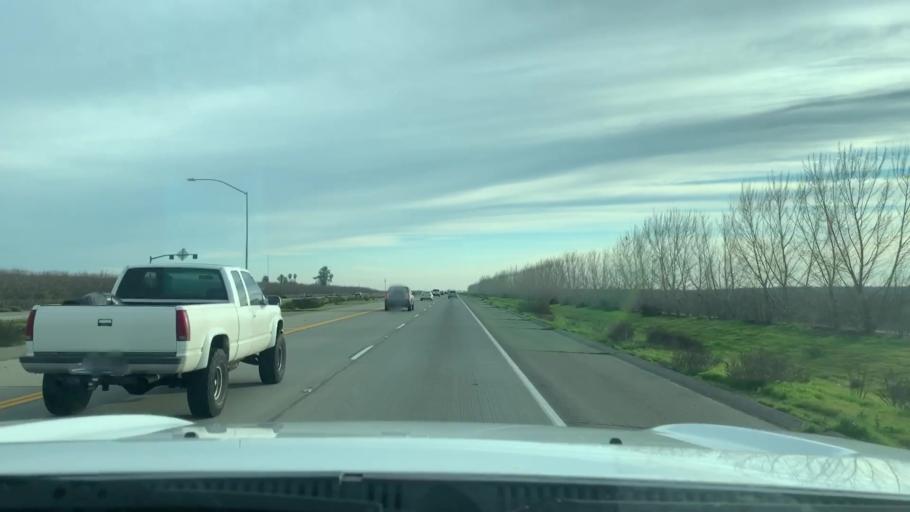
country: US
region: California
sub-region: Fresno County
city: Caruthers
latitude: 36.5167
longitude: -119.7864
